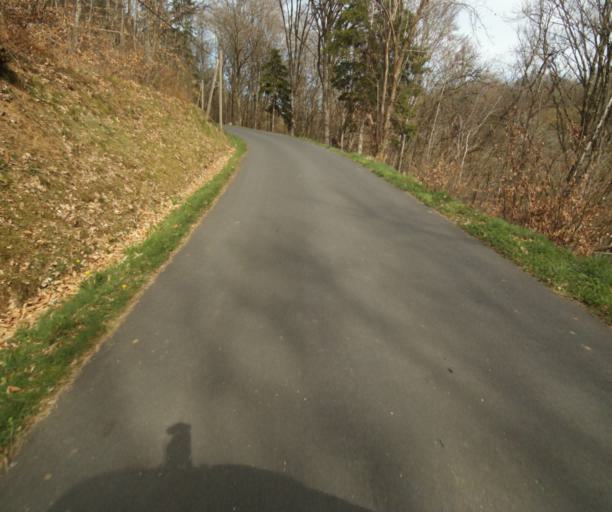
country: FR
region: Limousin
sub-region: Departement de la Correze
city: Correze
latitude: 45.3546
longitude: 1.8168
